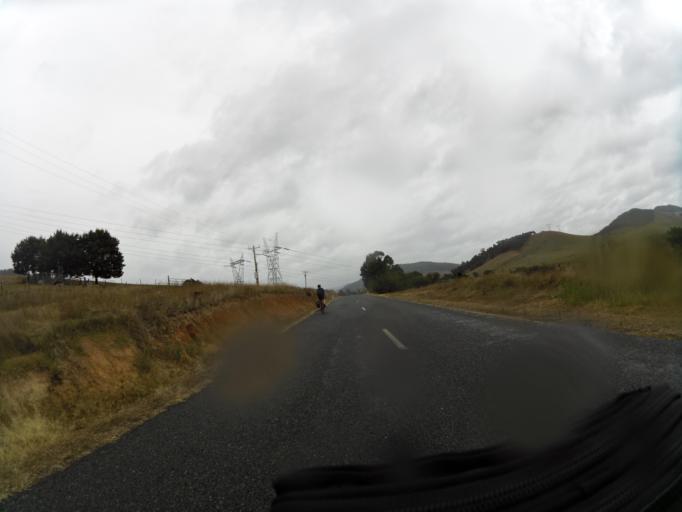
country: AU
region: New South Wales
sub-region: Greater Hume Shire
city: Holbrook
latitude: -36.2252
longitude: 147.6600
